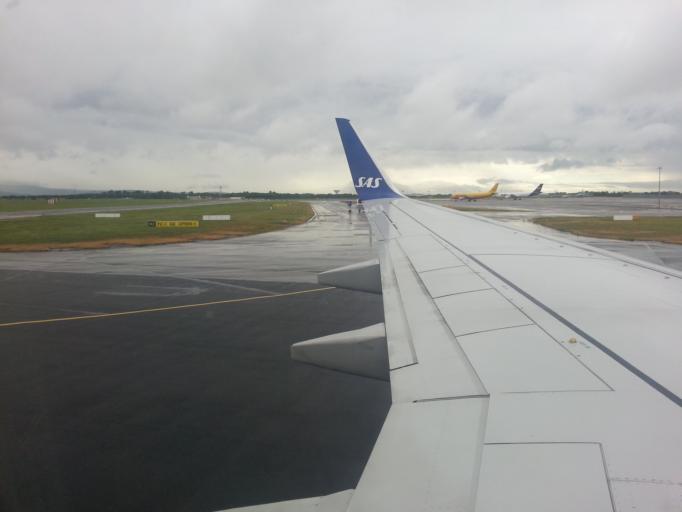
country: IE
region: Leinster
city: Ballymun
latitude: 53.4265
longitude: -6.2545
